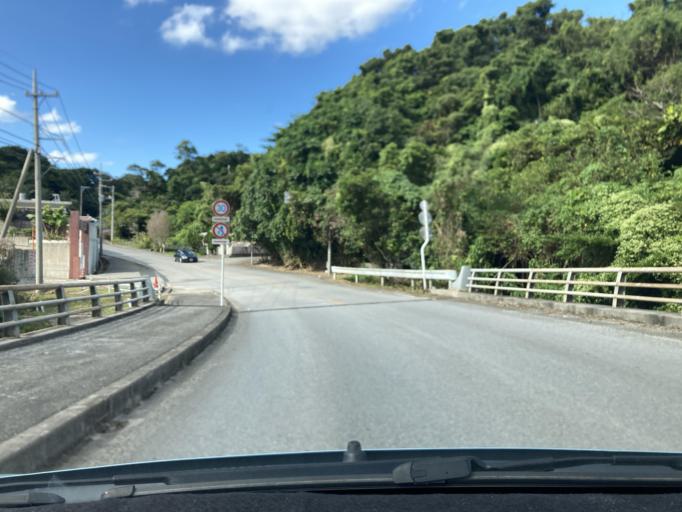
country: JP
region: Okinawa
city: Gushikawa
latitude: 26.3760
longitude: 127.8297
